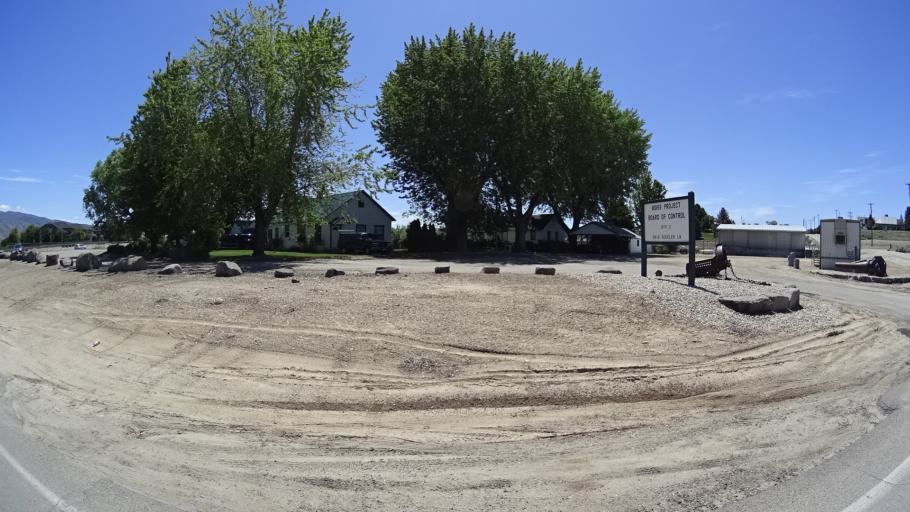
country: US
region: Idaho
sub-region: Ada County
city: Boise
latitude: 43.5677
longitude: -116.1833
